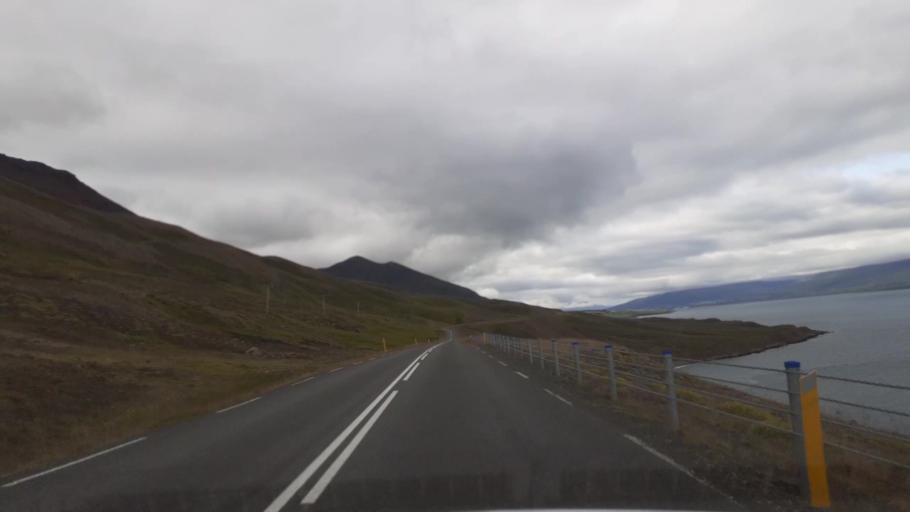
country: IS
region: Northeast
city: Akureyri
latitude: 65.8424
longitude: -18.0571
